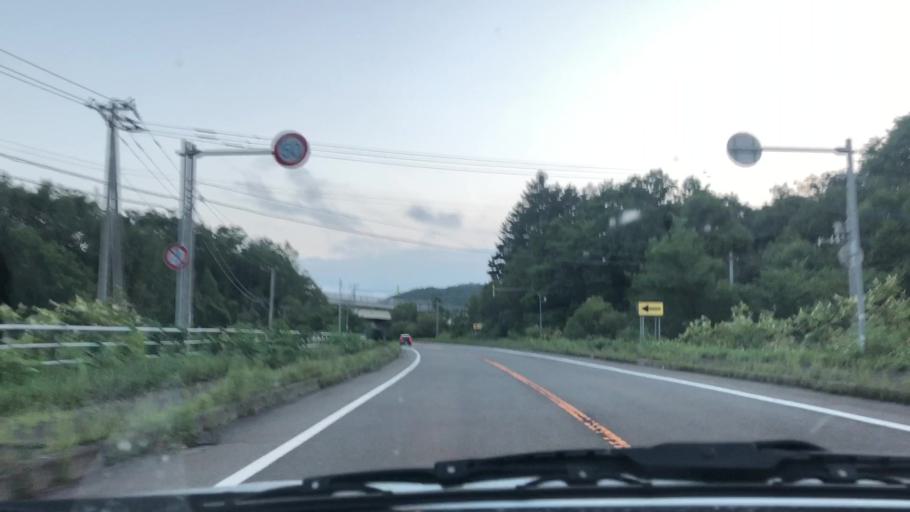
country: JP
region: Hokkaido
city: Chitose
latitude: 42.9173
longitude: 142.0294
